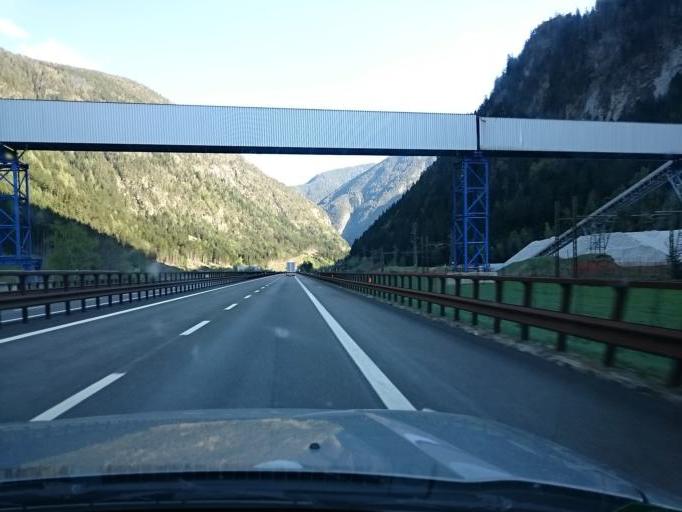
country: IT
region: Trentino-Alto Adige
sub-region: Bolzano
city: Campo di Trens
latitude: 46.8360
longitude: 11.5298
